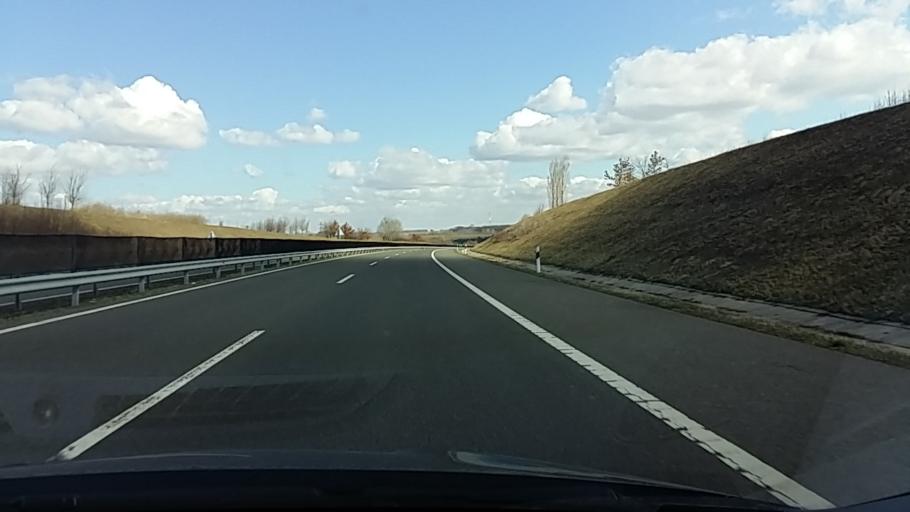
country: HU
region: Baranya
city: Boly
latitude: 45.9845
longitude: 18.4391
